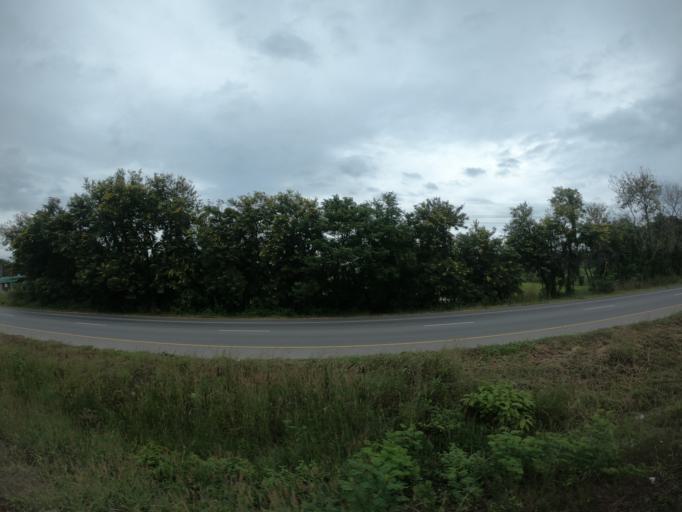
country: TH
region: Roi Et
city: Changhan
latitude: 16.0820
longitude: 103.5722
